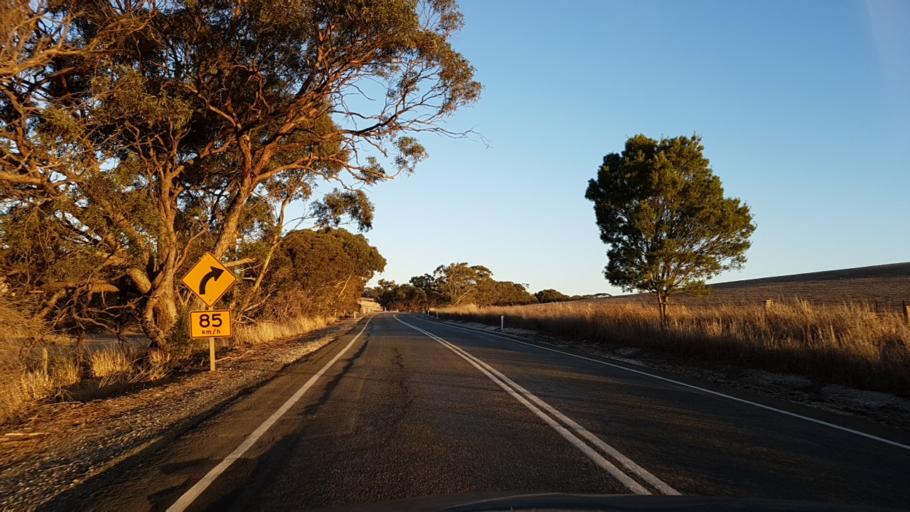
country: AU
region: South Australia
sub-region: Wakefield
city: Balaklava
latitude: -34.1564
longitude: 138.6947
